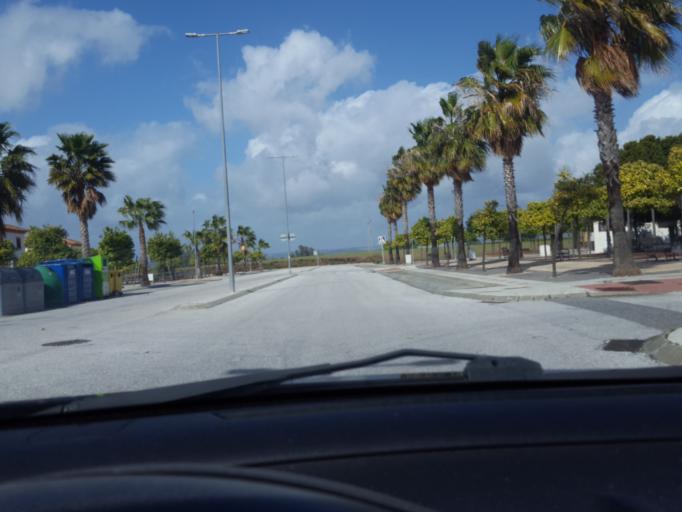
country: ES
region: Andalusia
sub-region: Provincia de Sevilla
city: Acala del Rio
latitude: 37.5143
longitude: -5.9881
